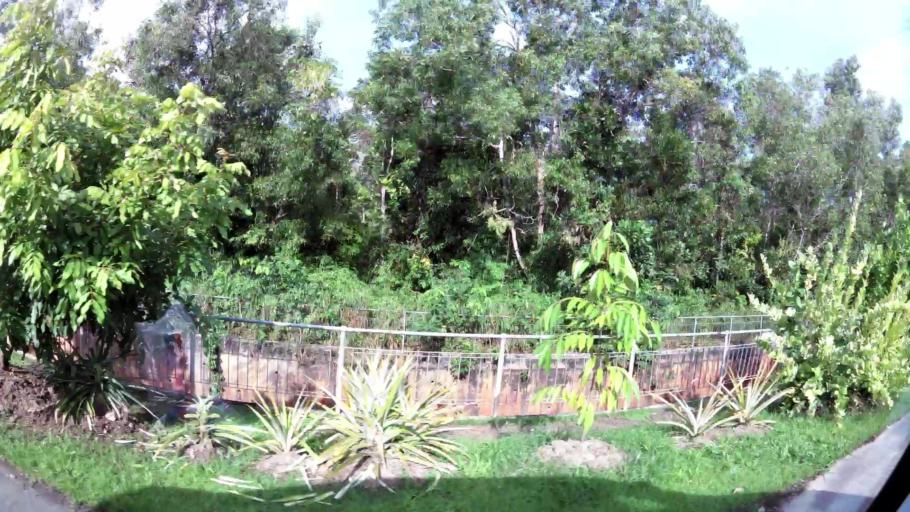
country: BN
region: Brunei and Muara
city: Bandar Seri Begawan
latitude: 4.9113
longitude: 114.8925
